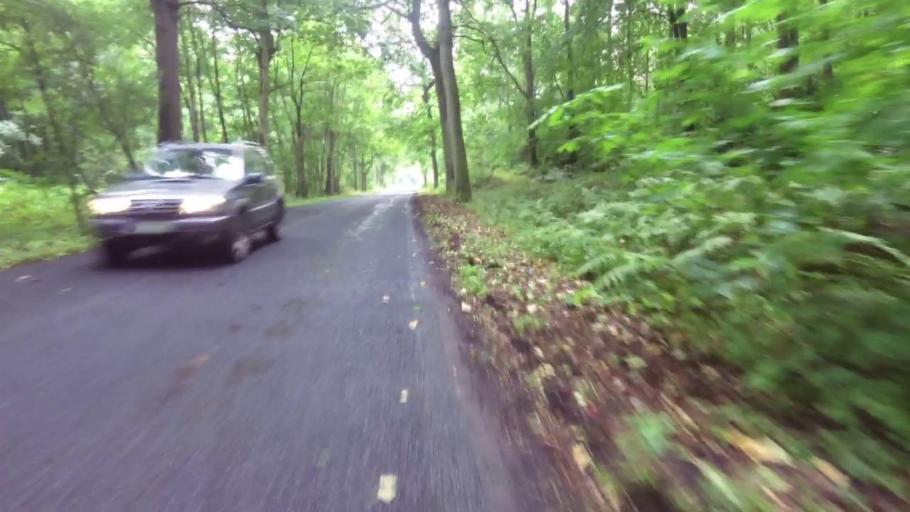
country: PL
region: West Pomeranian Voivodeship
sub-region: Powiat choszczenski
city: Choszczno
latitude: 53.2218
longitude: 15.3821
